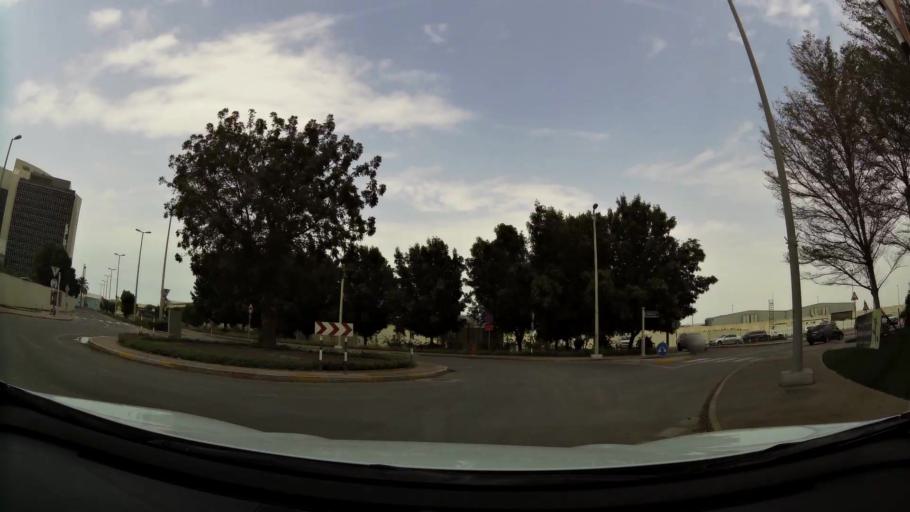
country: AE
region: Abu Dhabi
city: Abu Dhabi
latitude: 24.4213
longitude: 54.4605
